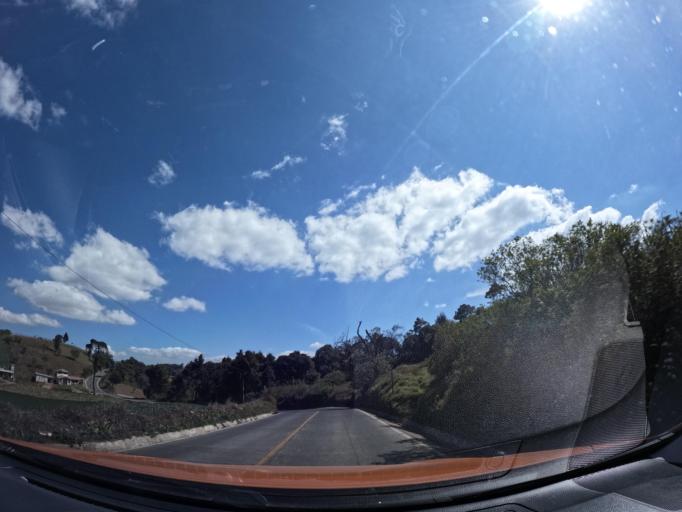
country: GT
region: Chimaltenango
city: Patzun
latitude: 14.6539
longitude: -91.0520
